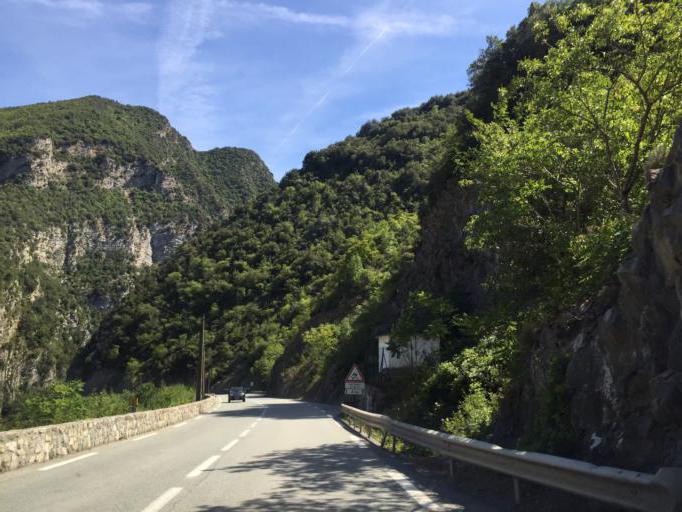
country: FR
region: Provence-Alpes-Cote d'Azur
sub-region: Departement des Alpes-Maritimes
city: Levens
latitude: 43.9224
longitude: 7.1858
